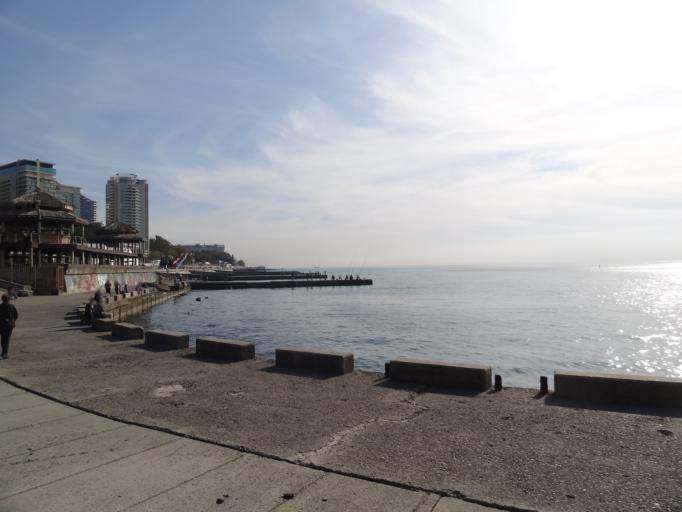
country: RU
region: Krasnodarskiy
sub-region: Sochi City
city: Sochi
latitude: 43.5790
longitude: 39.7183
